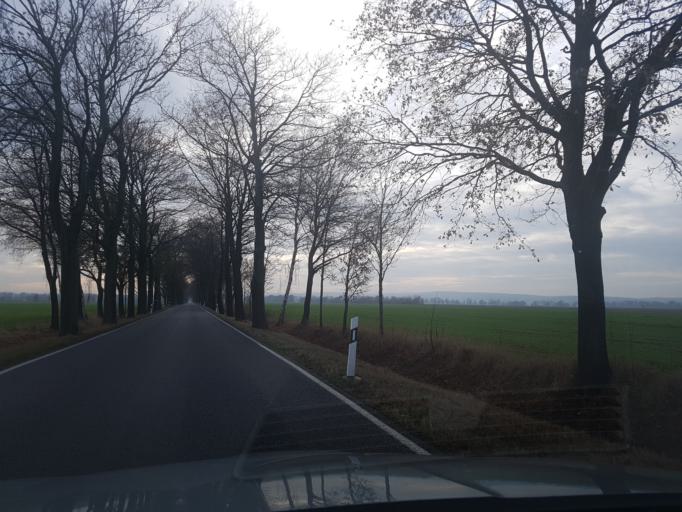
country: DE
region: Brandenburg
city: Plessa
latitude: 51.4277
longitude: 13.6239
